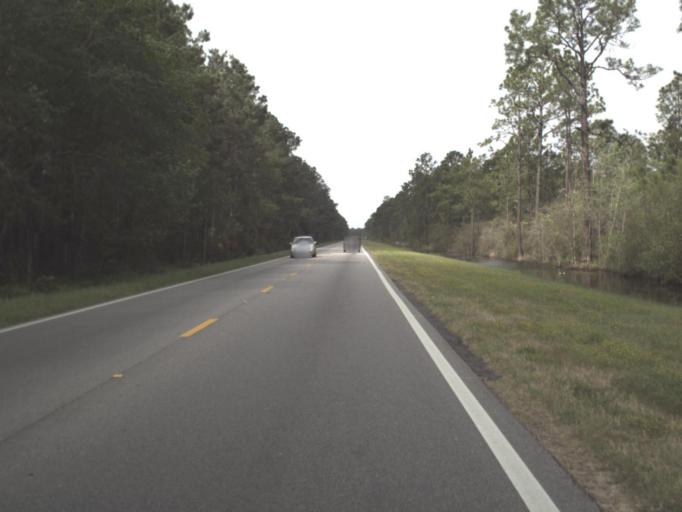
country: US
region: Florida
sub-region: Escambia County
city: Myrtle Grove
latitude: 30.3552
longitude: -87.3726
